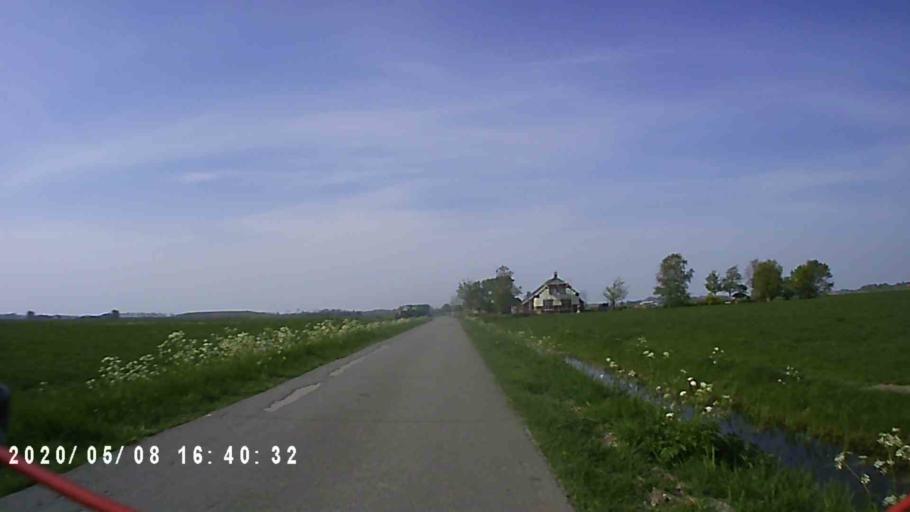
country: NL
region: Groningen
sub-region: Gemeente Bedum
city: Bedum
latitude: 53.3703
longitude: 6.6051
